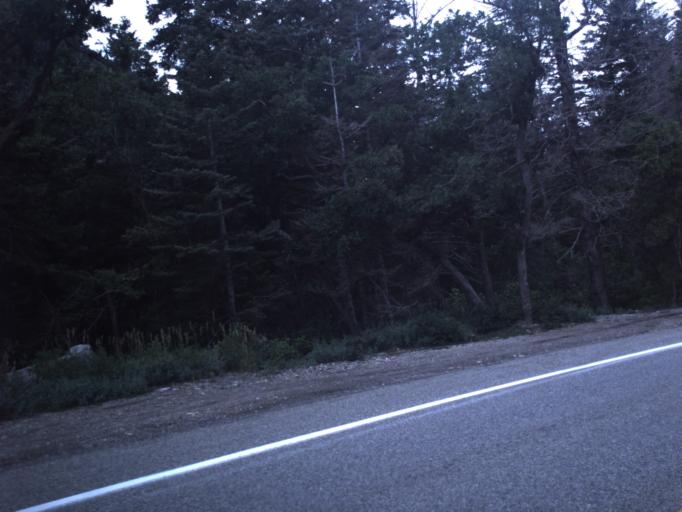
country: US
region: Utah
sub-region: Salt Lake County
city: Granite
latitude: 40.5719
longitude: -111.7294
